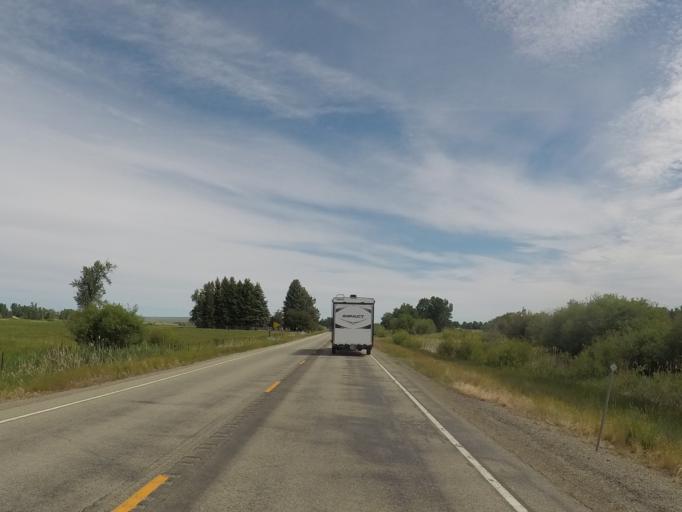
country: US
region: Montana
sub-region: Carbon County
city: Red Lodge
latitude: 45.3447
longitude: -109.1771
